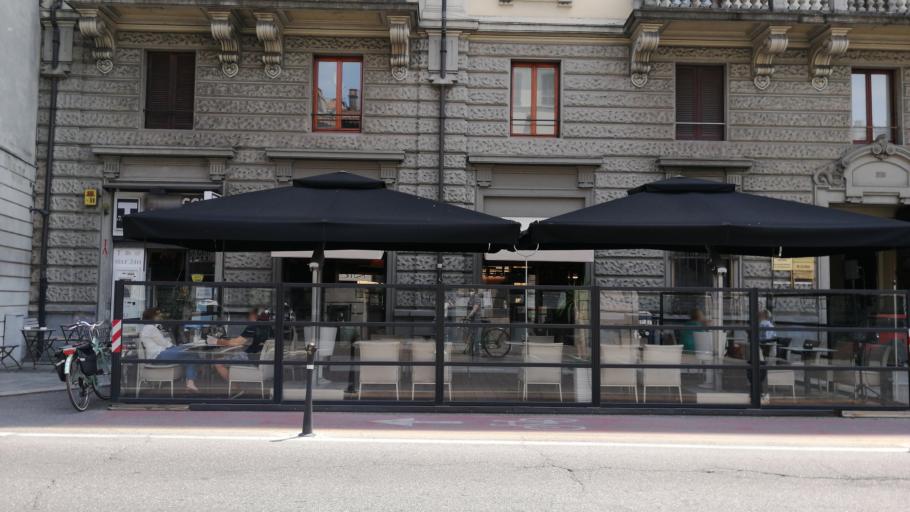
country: IT
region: Emilia-Romagna
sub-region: Provincia di Piacenza
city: Piacenza
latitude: 45.0478
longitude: 9.6875
